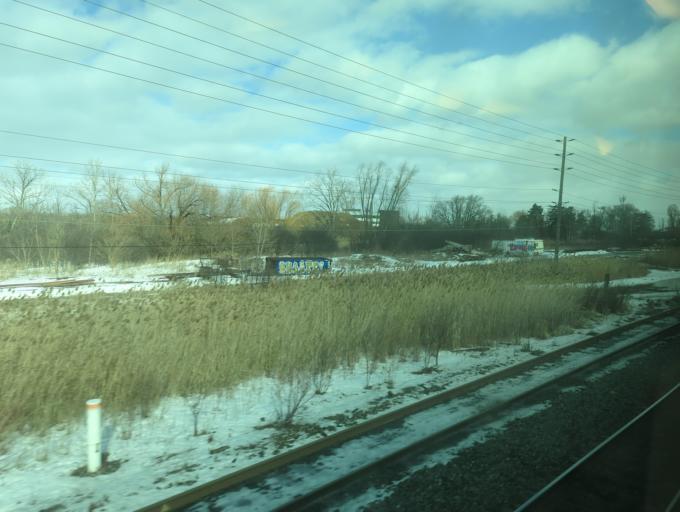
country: CA
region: Ontario
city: Oakville
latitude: 43.4623
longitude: -79.6758
